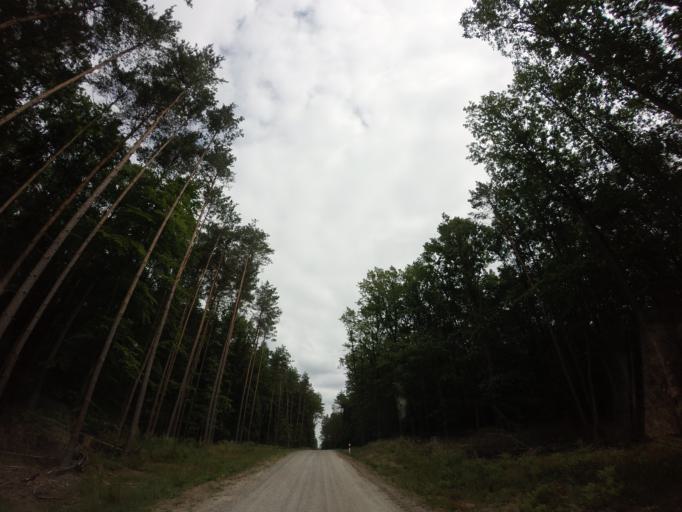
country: PL
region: Lubusz
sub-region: Powiat strzelecko-drezdenecki
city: Stare Kurowo
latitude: 52.8929
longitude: 15.6468
